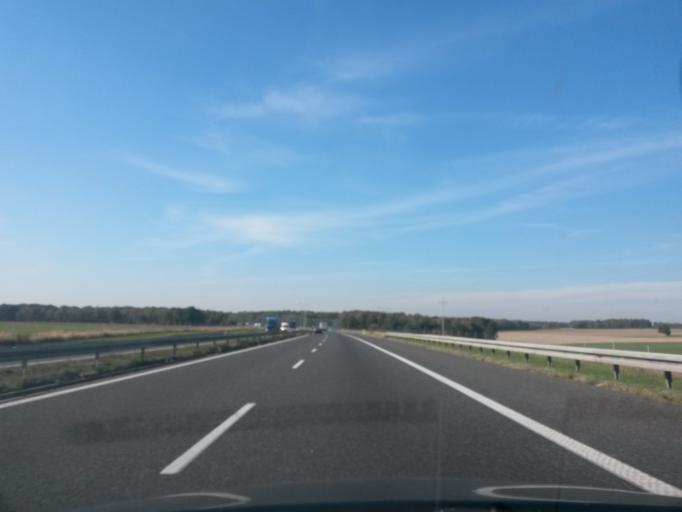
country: PL
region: Opole Voivodeship
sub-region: Powiat strzelecki
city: Ujazd
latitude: 50.4198
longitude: 18.3994
